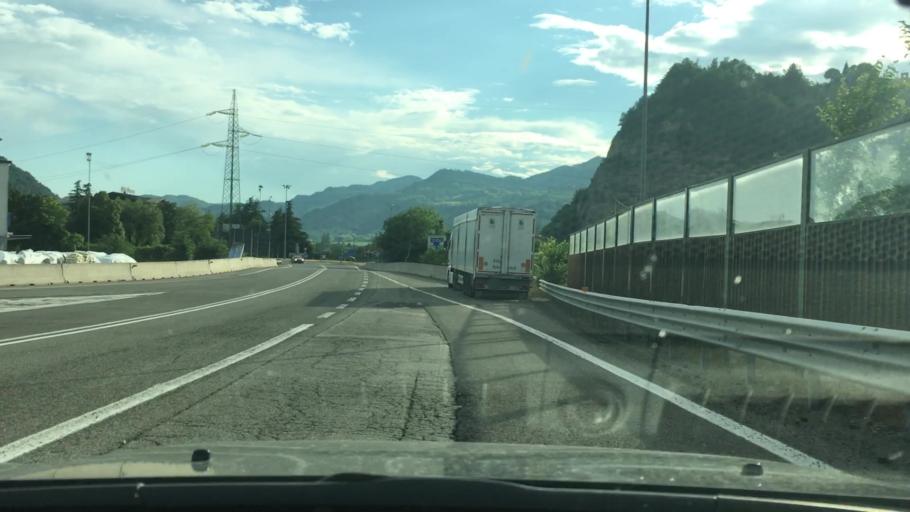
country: IT
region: Emilia-Romagna
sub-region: Provincia di Bologna
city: Sasso Marconi
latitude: 44.3894
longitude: 11.2496
